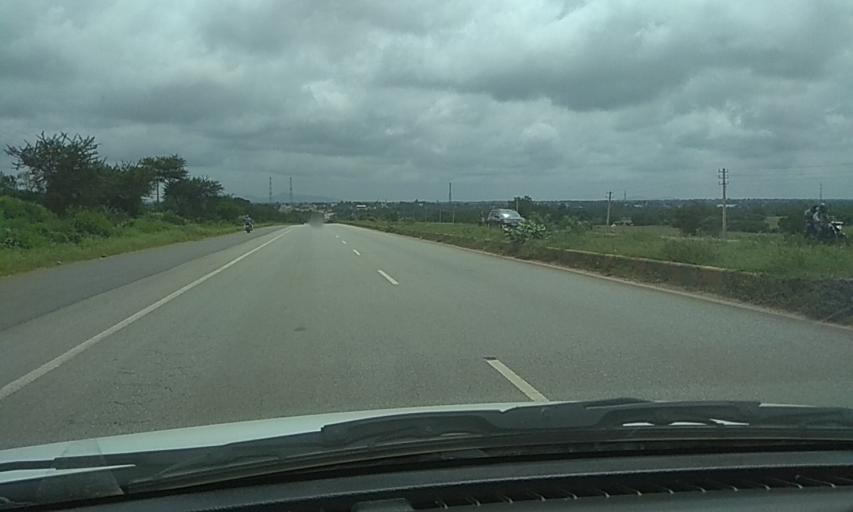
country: IN
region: Karnataka
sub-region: Davanagere
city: Mayakonda
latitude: 14.3693
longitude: 76.1761
